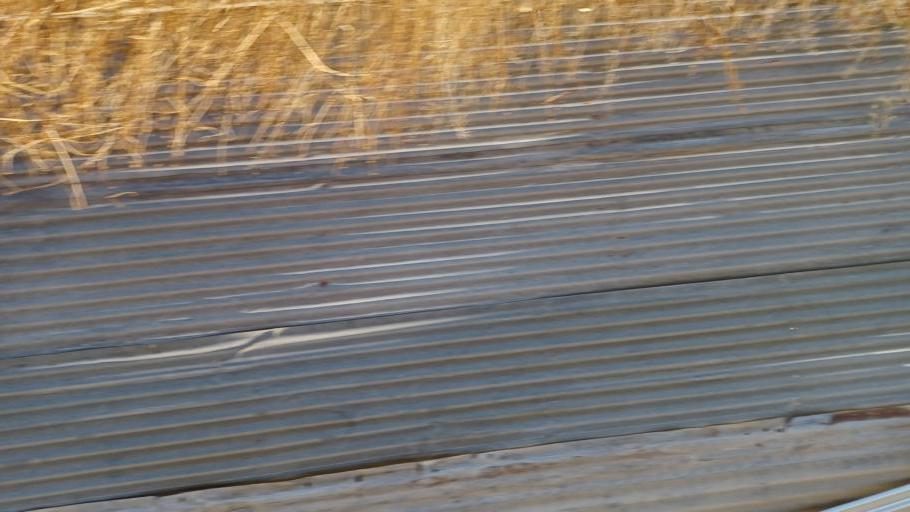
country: CY
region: Larnaka
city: Psevdas
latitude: 34.9376
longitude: 33.5264
